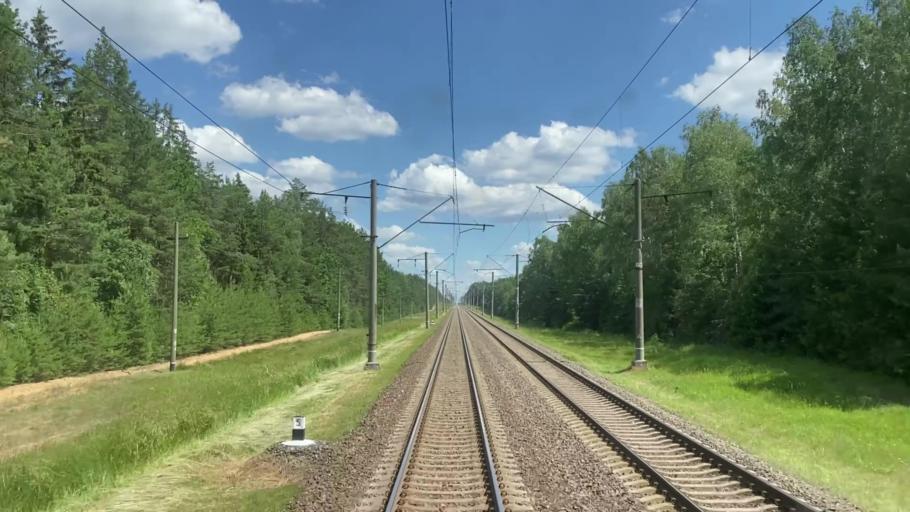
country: BY
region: Brest
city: Ivatsevichy
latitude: 52.8540
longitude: 25.5756
